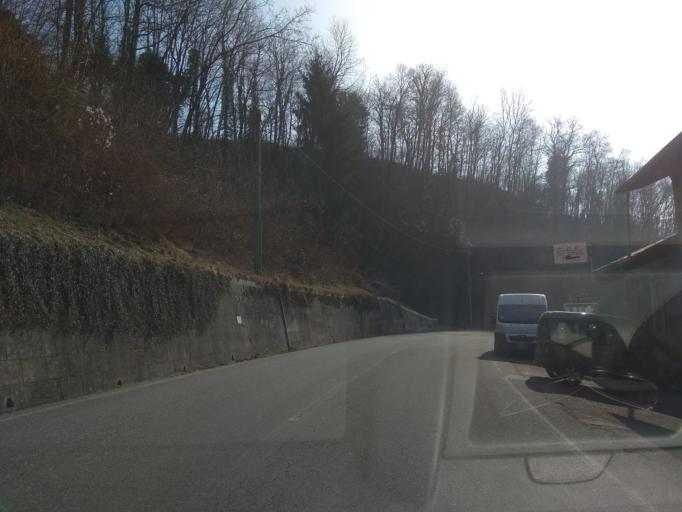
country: IT
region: Piedmont
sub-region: Provincia di Biella
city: Mosso
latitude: 45.6512
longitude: 8.1444
